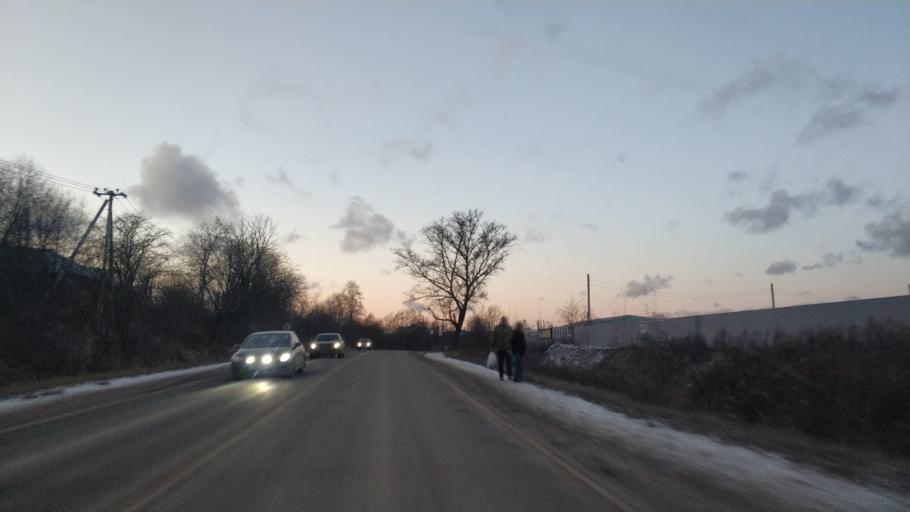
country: RU
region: St.-Petersburg
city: Pontonnyy
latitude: 59.8082
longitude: 30.6161
